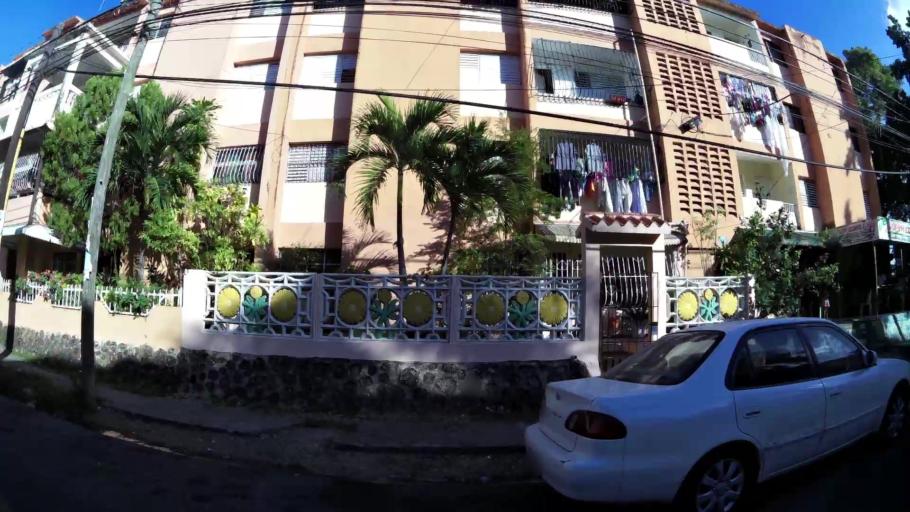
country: DO
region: Nacional
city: Santo Domingo
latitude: 18.4949
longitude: -69.9672
